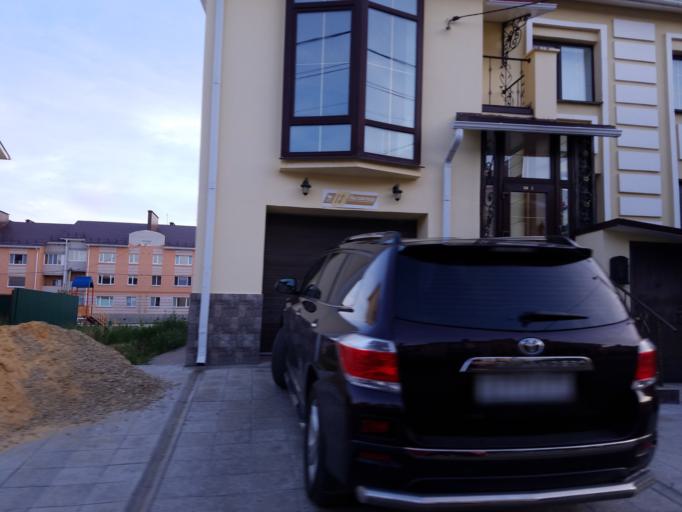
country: RU
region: Orjol
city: Znamenka
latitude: 52.9117
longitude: 36.0073
